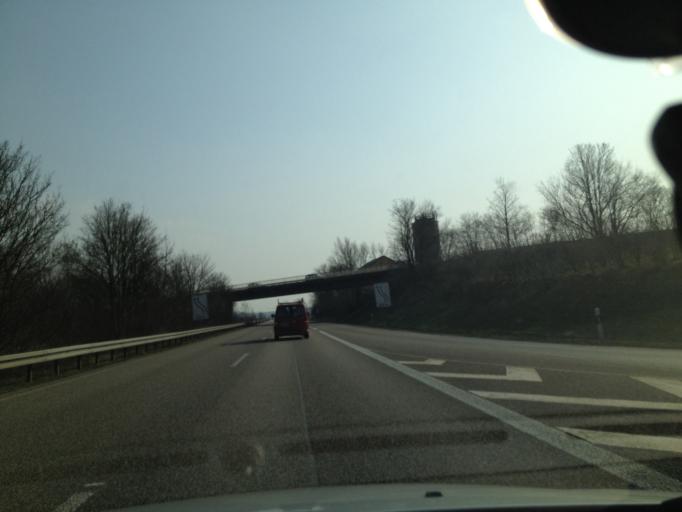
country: DE
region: Hesse
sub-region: Regierungsbezirk Darmstadt
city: Langenselbold
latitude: 50.1825
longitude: 9.0123
